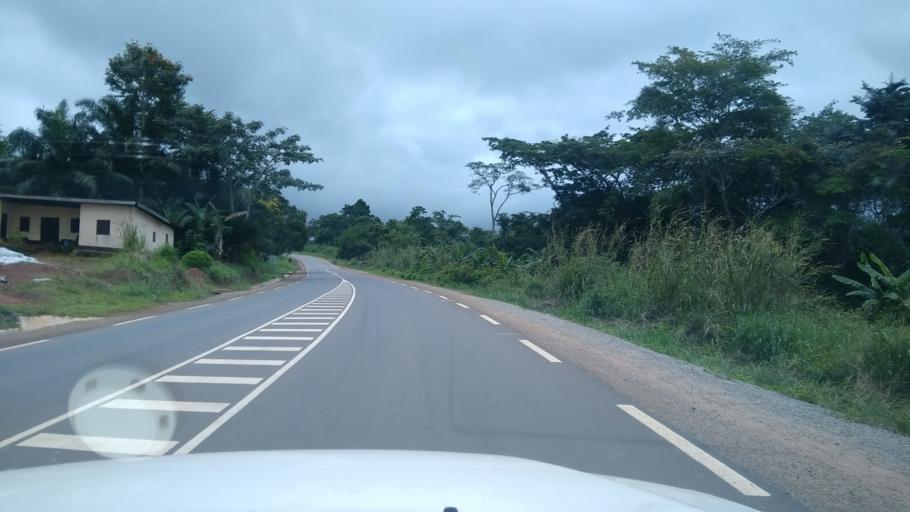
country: CM
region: Centre
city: Mbalmayo
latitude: 3.6033
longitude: 11.5269
